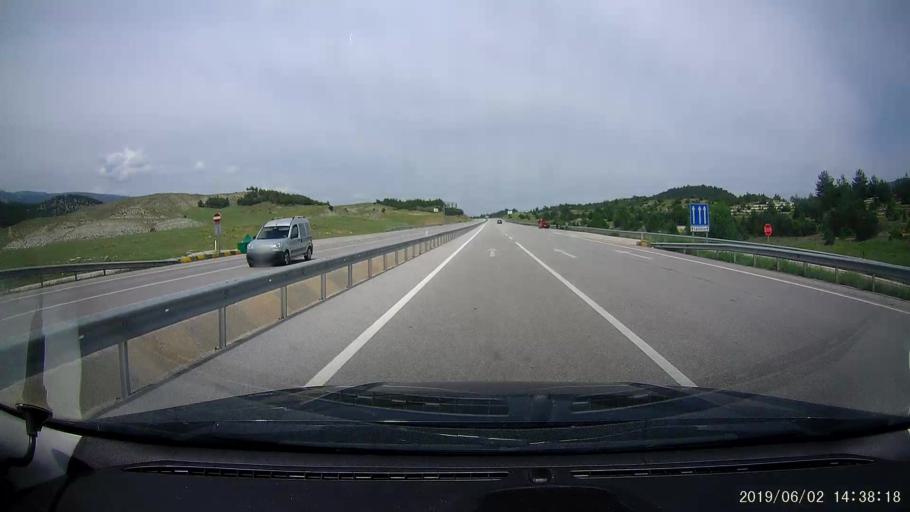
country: TR
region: Corum
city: Hacihamza
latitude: 41.0530
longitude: 34.2773
